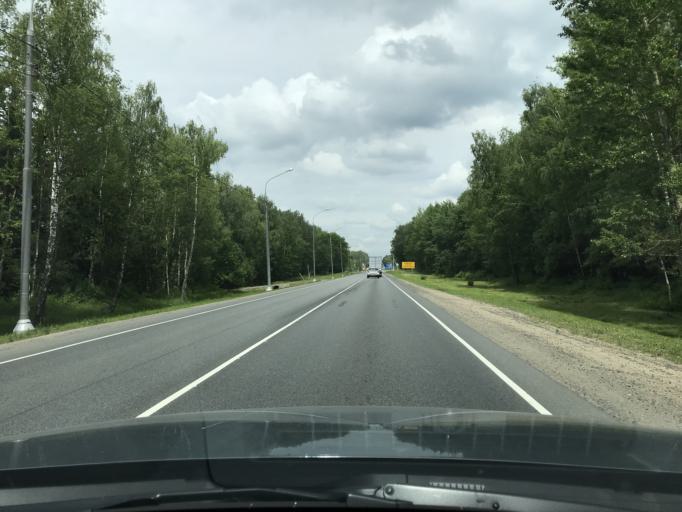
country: RU
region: Moskovskaya
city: Dorokhovo
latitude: 55.3792
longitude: 36.4030
